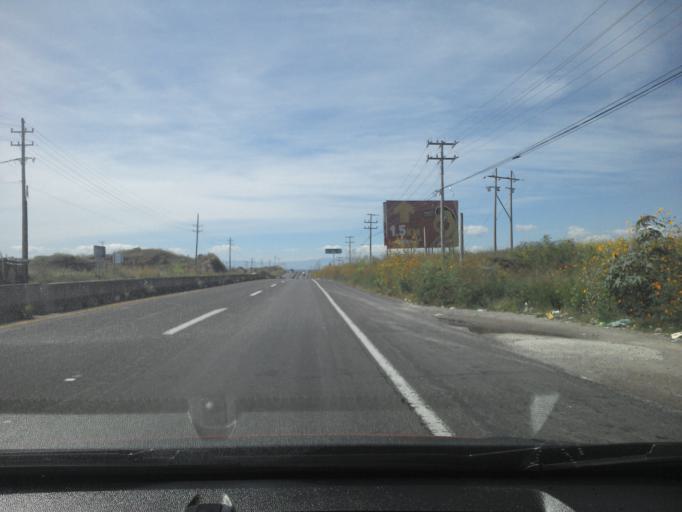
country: MX
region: Jalisco
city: Tala
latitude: 20.6767
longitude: -103.7039
